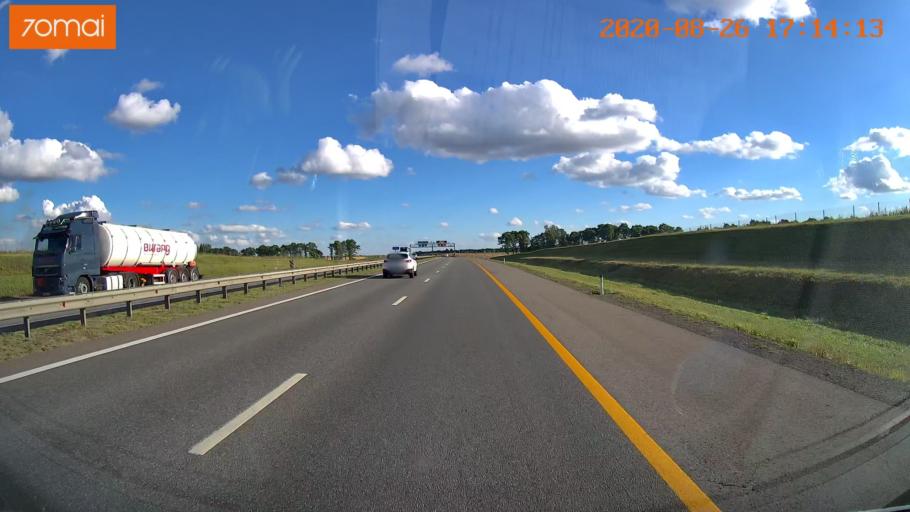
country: RU
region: Tula
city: Volovo
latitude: 53.6571
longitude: 38.0525
